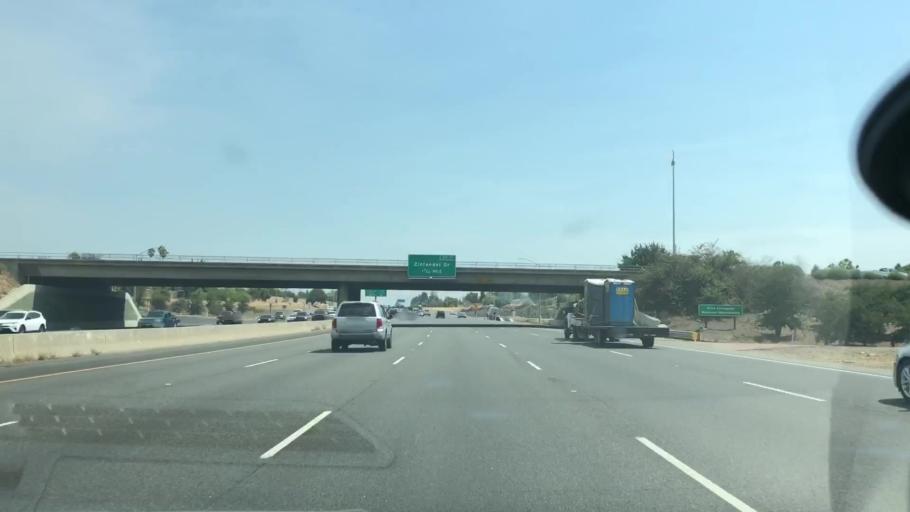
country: US
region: California
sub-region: Sacramento County
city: Rancho Cordova
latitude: 38.5788
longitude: -121.3101
